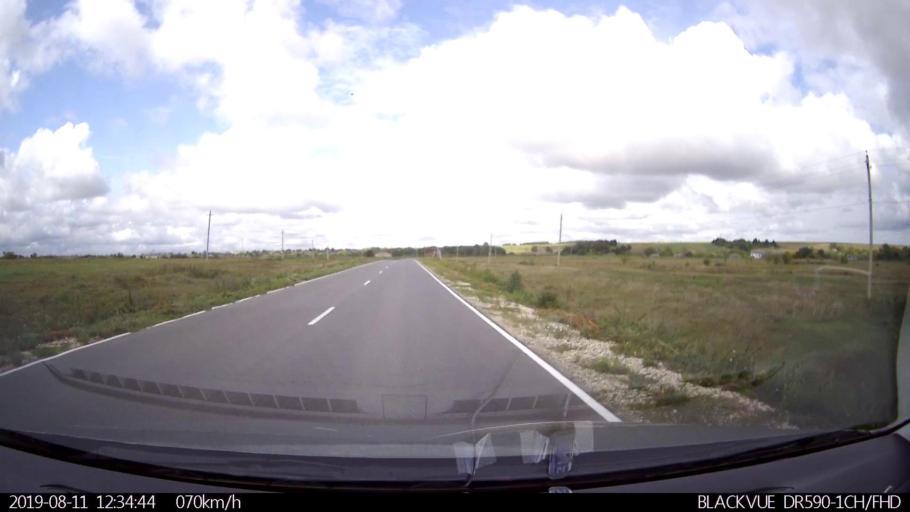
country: RU
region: Ulyanovsk
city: Ignatovka
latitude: 53.8191
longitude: 47.8389
